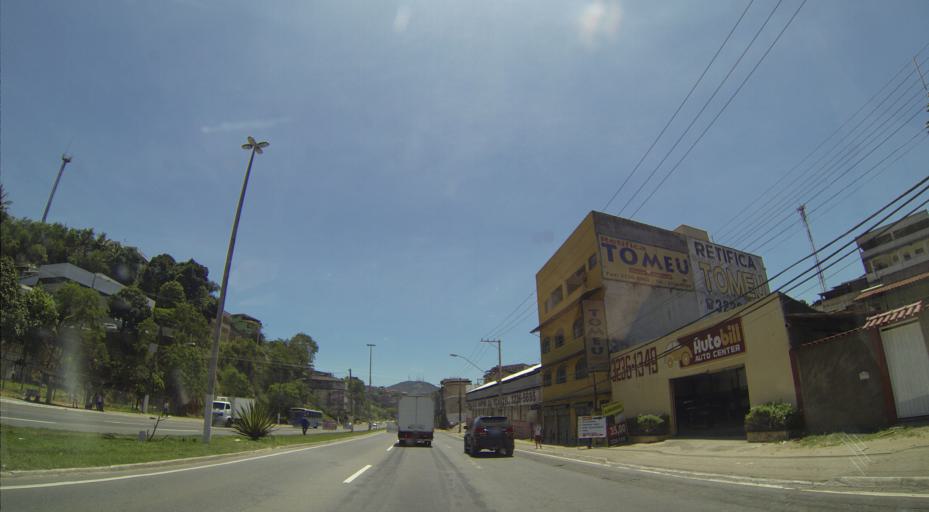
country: BR
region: Espirito Santo
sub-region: Vitoria
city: Vitoria
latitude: -20.3337
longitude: -40.3688
